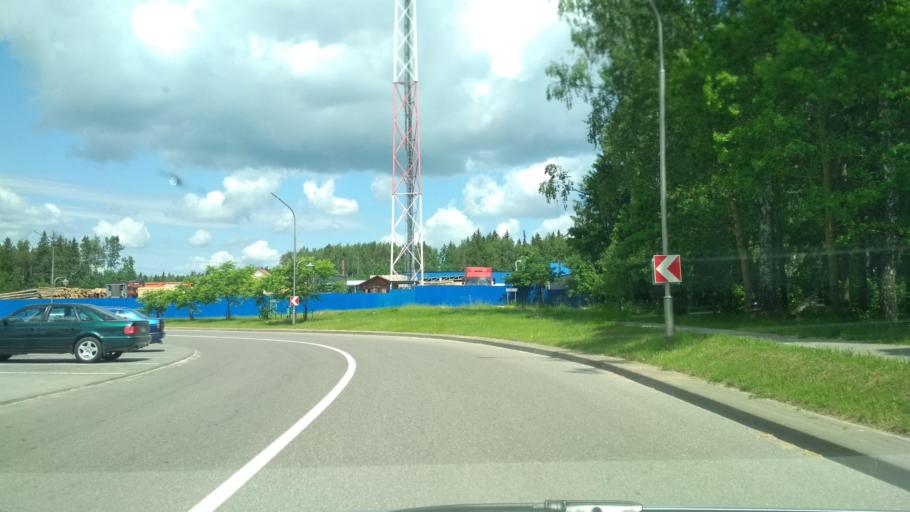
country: BY
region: Grodnenskaya
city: Astravyets
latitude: 54.6173
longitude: 25.9826
